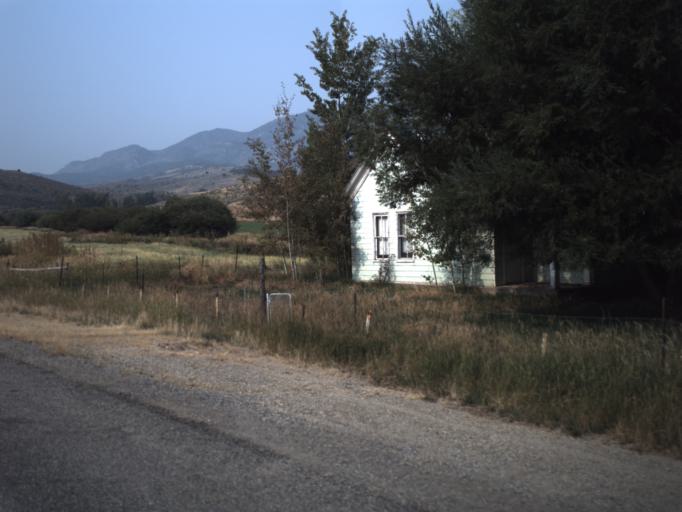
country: US
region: Utah
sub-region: Summit County
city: Coalville
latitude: 40.9910
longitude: -111.5259
